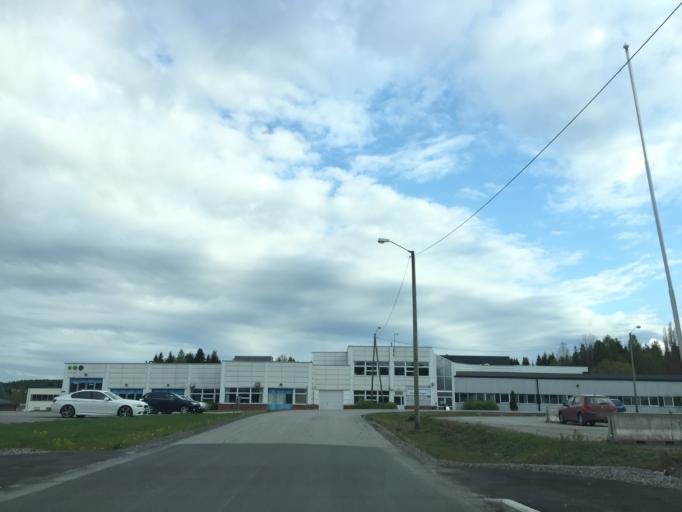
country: NO
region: Hedmark
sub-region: Kongsvinger
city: Kongsvinger
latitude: 60.1755
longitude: 12.0188
